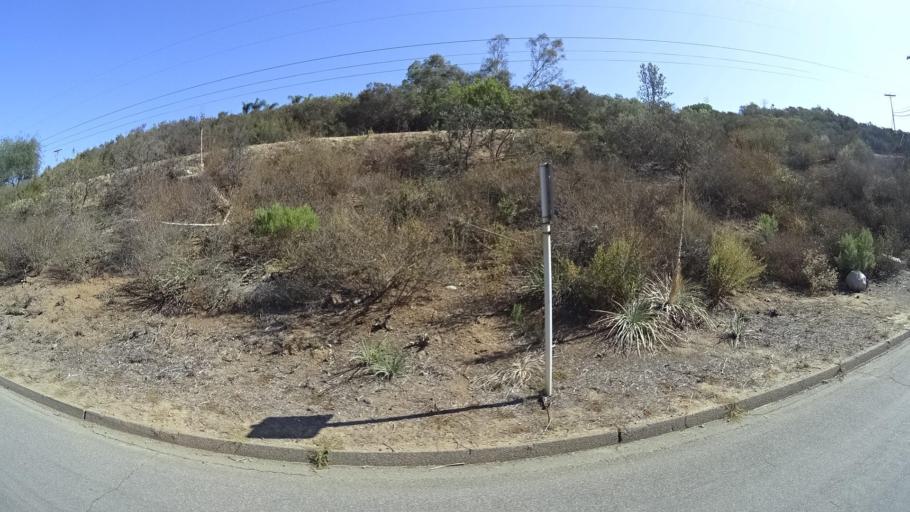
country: US
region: California
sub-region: San Diego County
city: Hidden Meadows
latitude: 33.2262
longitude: -117.1202
